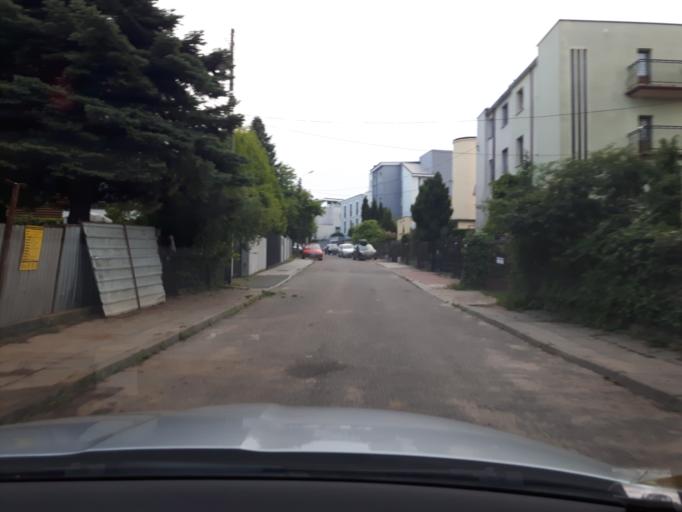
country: PL
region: Pomeranian Voivodeship
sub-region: Sopot
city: Sopot
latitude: 54.4781
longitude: 18.5570
